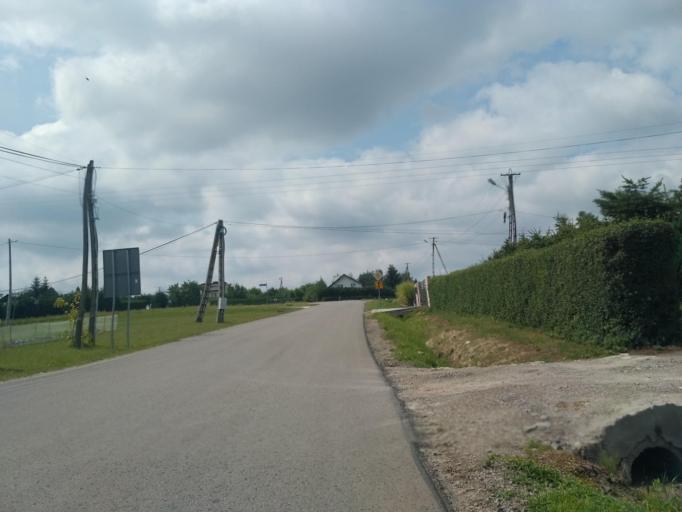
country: PL
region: Subcarpathian Voivodeship
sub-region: Powiat lancucki
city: Kraczkowa
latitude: 50.0153
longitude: 22.1636
